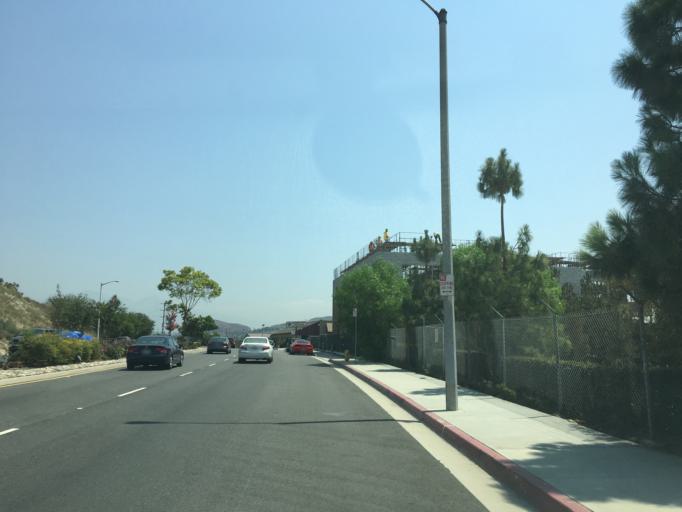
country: US
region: California
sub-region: Los Angeles County
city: Diamond Bar
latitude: 34.0307
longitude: -117.8284
